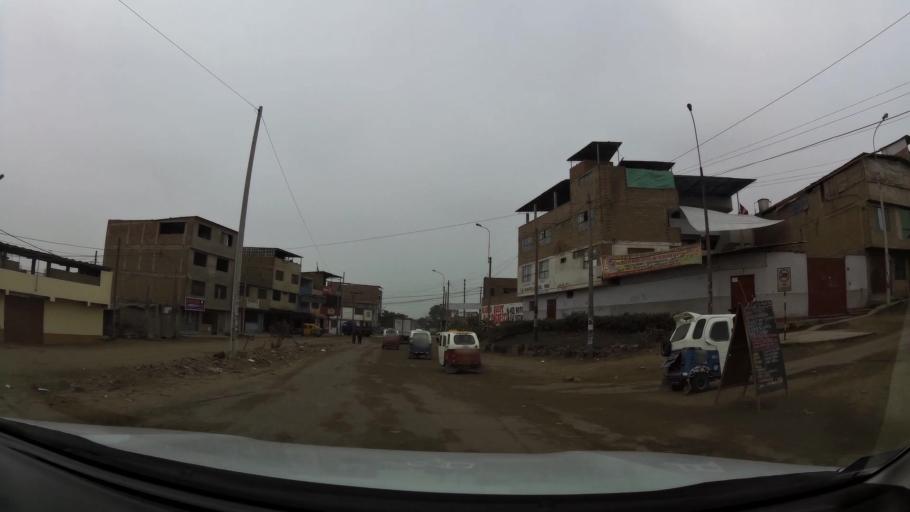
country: PE
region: Lima
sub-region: Lima
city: Surco
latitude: -12.1924
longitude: -76.9330
